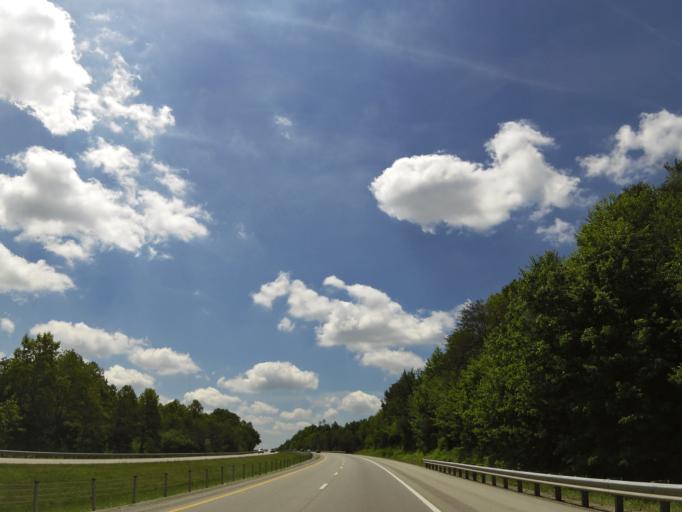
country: US
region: Kentucky
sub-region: Whitley County
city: Corbin
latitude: 36.8835
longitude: -84.1510
